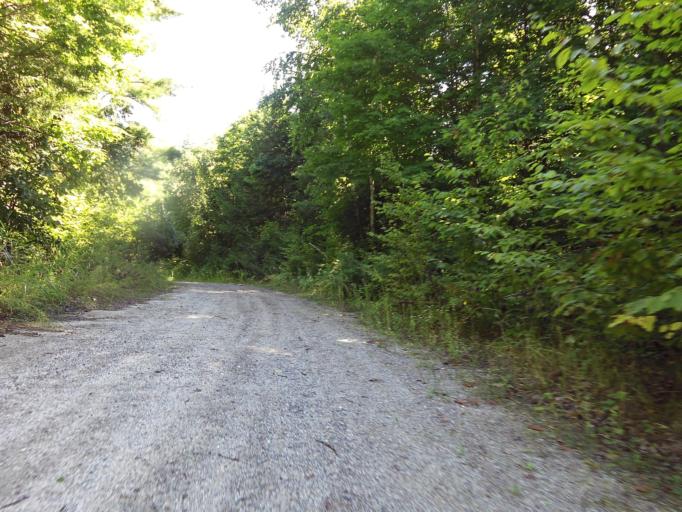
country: CA
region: Ontario
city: Arnprior
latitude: 45.1621
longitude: -76.4887
